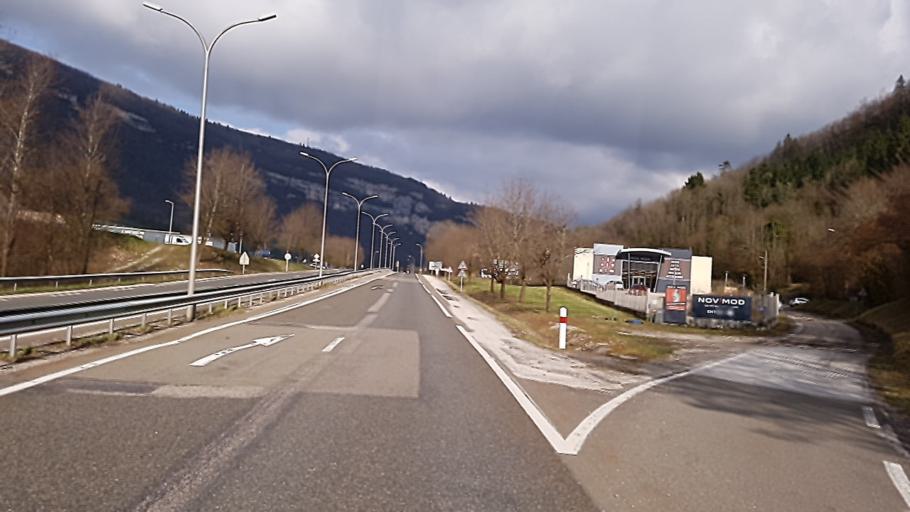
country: FR
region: Franche-Comte
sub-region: Departement du Jura
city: Saint-Lupicin
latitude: 46.3777
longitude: 5.8161
